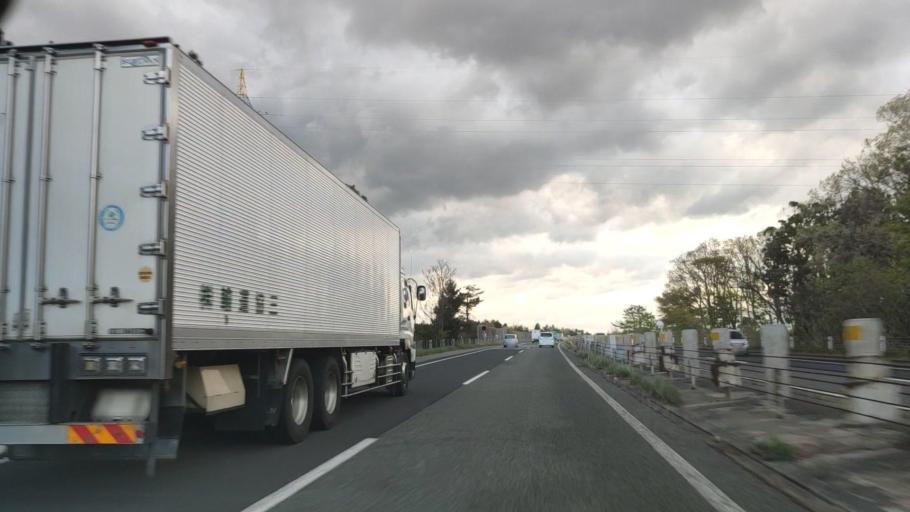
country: JP
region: Iwate
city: Kitakami
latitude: 39.3228
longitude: 141.0896
